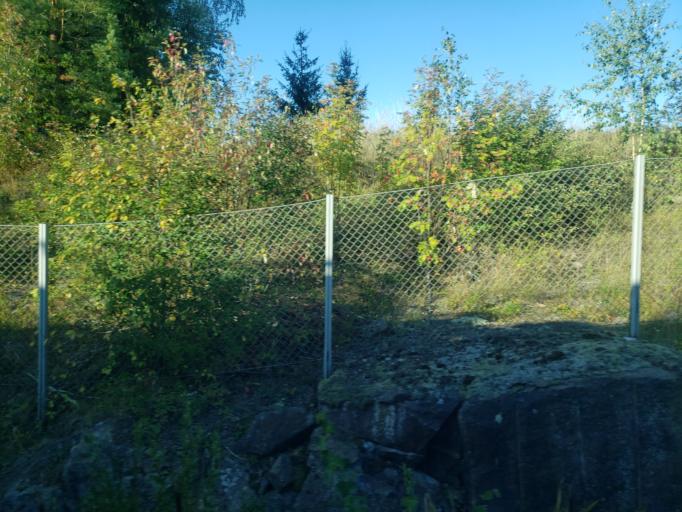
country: FI
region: South Karelia
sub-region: Lappeenranta
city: Lappeenranta
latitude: 60.8692
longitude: 28.2835
